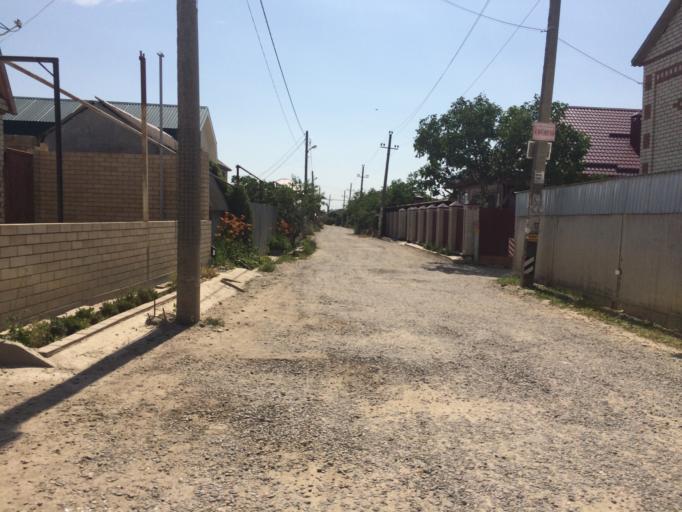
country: RU
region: Stavropol'skiy
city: Tatarka
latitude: 44.9875
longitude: 41.9413
